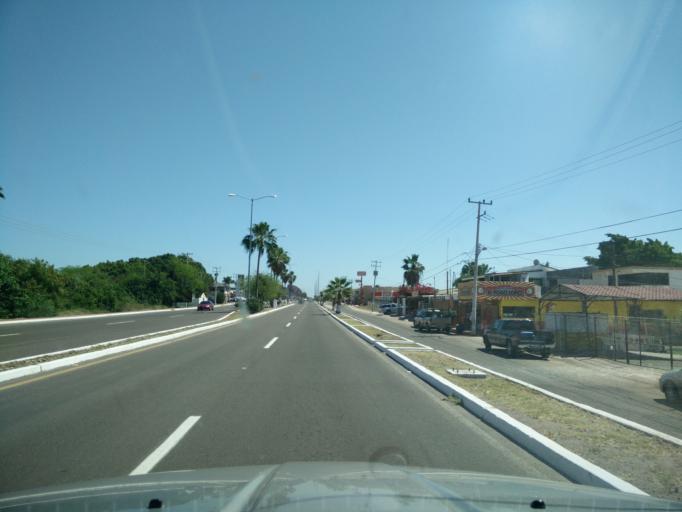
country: MX
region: Sonora
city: Heroica Guaymas
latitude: 27.9578
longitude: -111.0422
